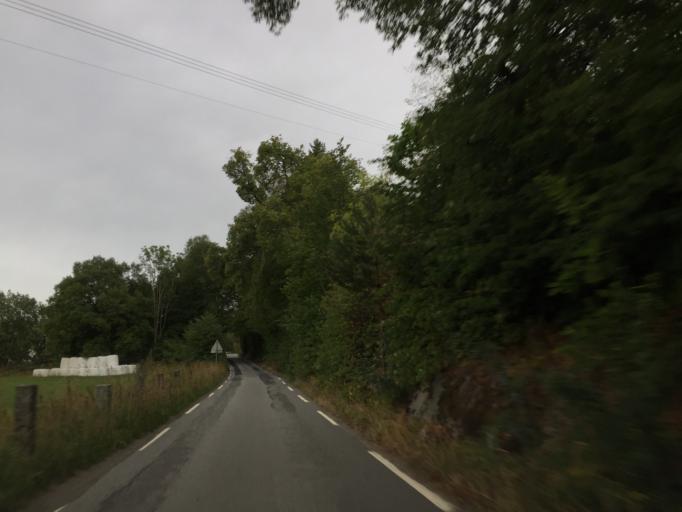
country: NO
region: Ostfold
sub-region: Hvaler
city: Skjaerhalden
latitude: 59.0500
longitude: 11.0033
